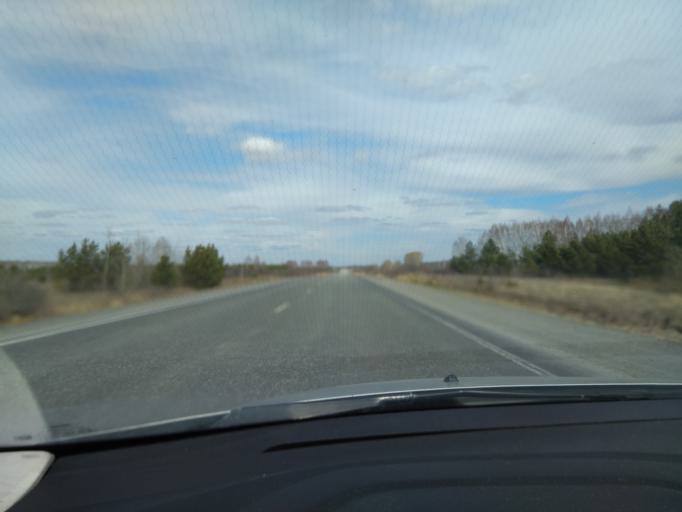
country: RU
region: Sverdlovsk
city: Obukhovskoye
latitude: 56.8282
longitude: 62.5610
